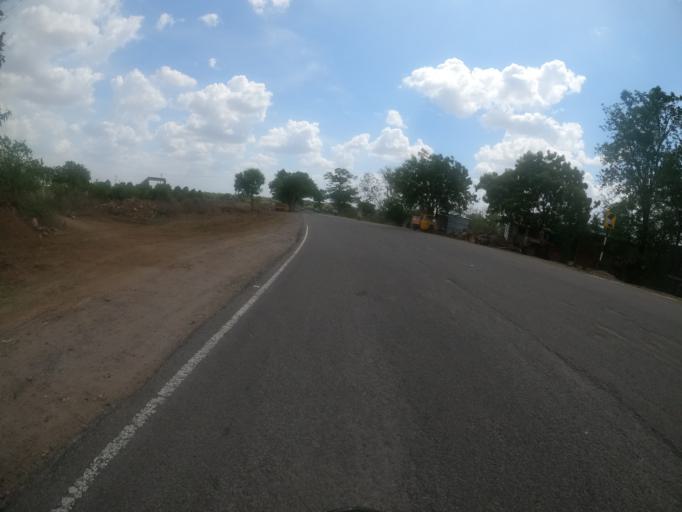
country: IN
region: Telangana
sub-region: Rangareddi
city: Sriramnagar
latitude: 17.3124
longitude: 78.1725
